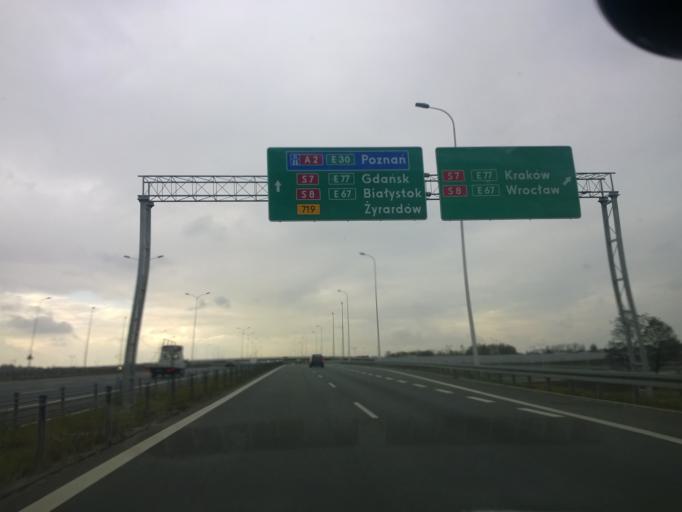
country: PL
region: Masovian Voivodeship
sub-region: Powiat pruszkowski
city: Nowe Grocholice
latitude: 52.1728
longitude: 20.9144
